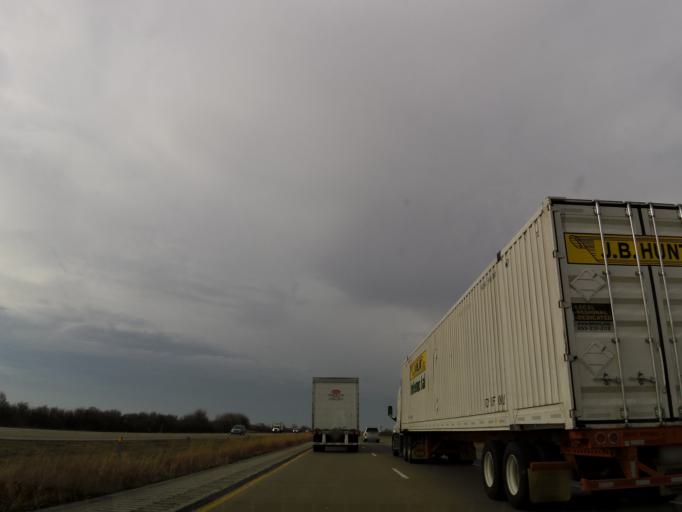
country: US
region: Iowa
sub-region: Scott County
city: Walcott
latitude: 41.6096
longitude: -90.7484
